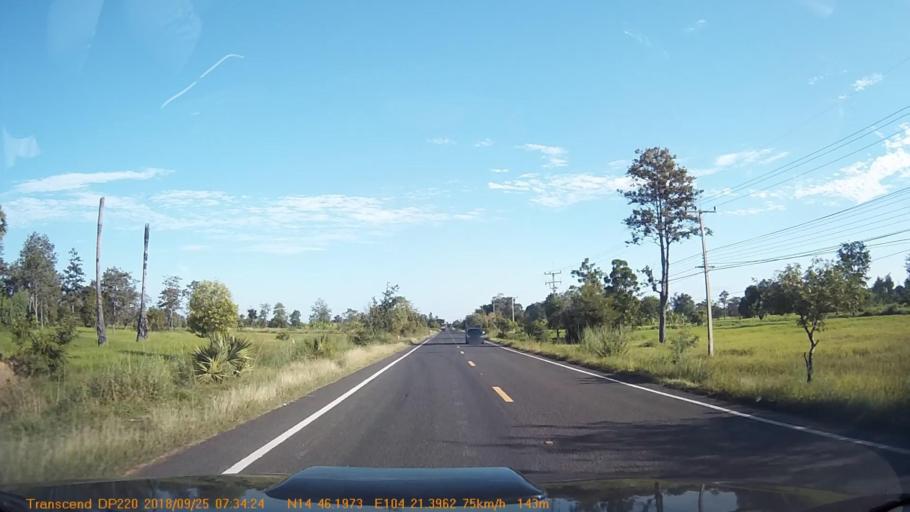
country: TH
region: Sisaket
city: Phrai Bueng
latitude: 14.7705
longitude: 104.3565
